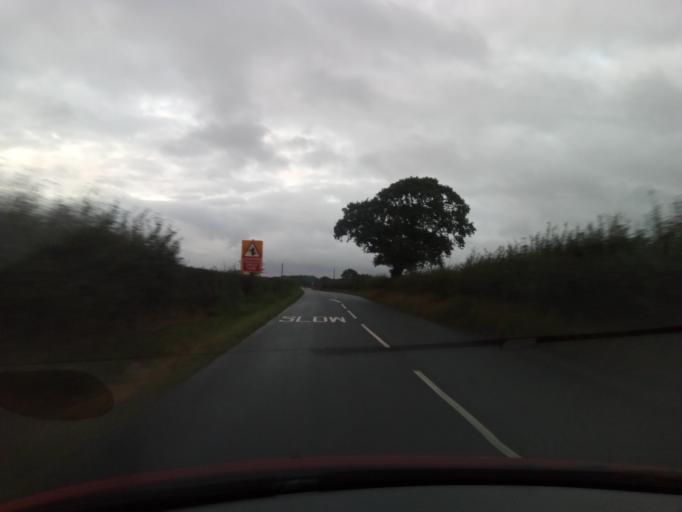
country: GB
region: England
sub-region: Darlington
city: Denton
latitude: 54.5624
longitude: -1.6764
